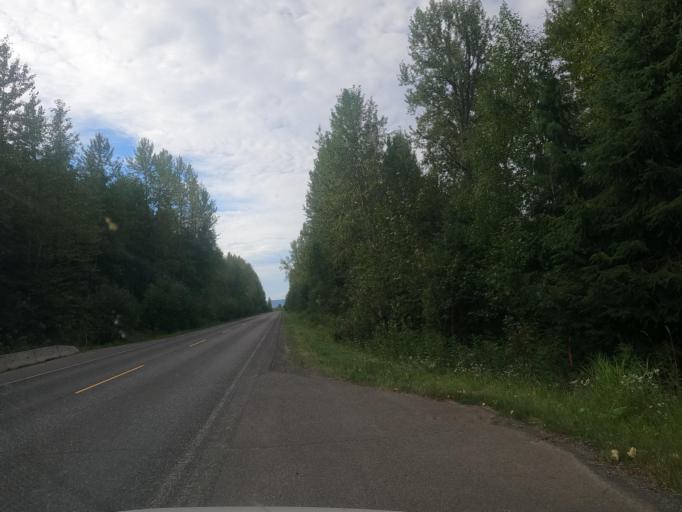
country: CA
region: British Columbia
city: Terrace
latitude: 55.3228
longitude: -128.0902
